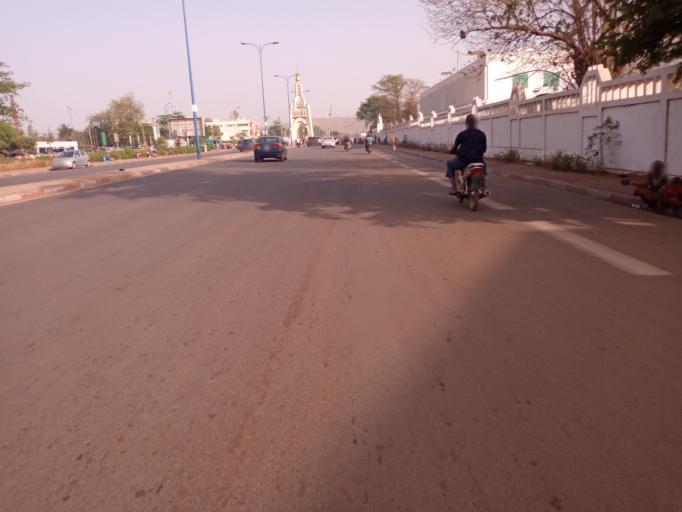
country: ML
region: Bamako
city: Bamako
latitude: 12.6358
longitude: -8.0038
